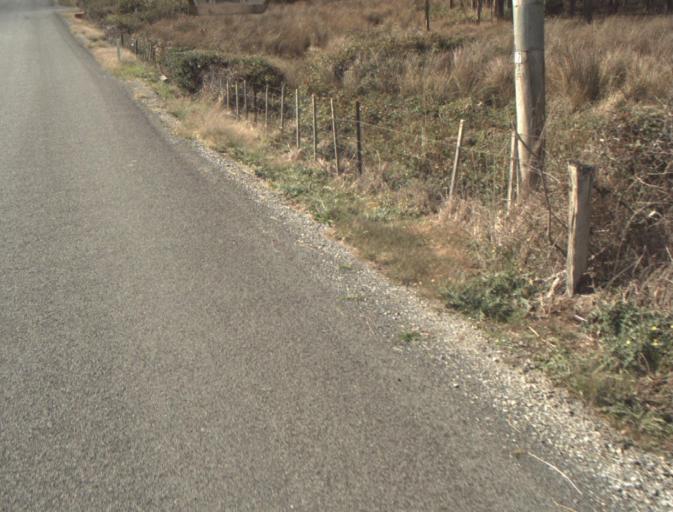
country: AU
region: Tasmania
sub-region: Launceston
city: Mayfield
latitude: -41.2394
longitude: 147.2335
